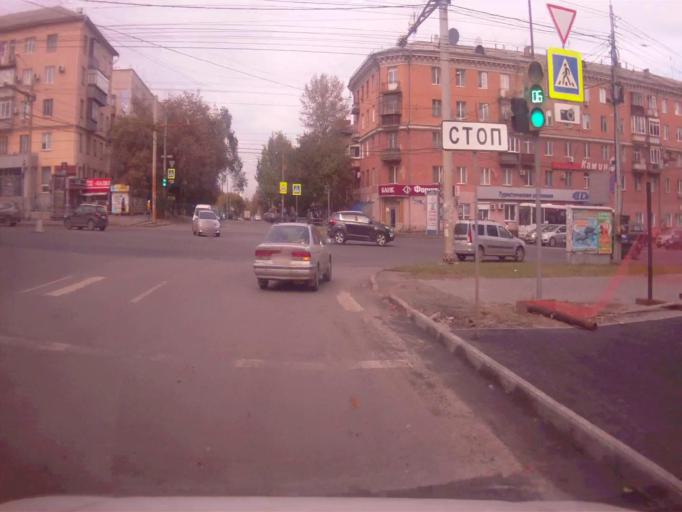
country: RU
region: Chelyabinsk
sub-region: Gorod Chelyabinsk
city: Chelyabinsk
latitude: 55.1605
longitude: 61.4217
